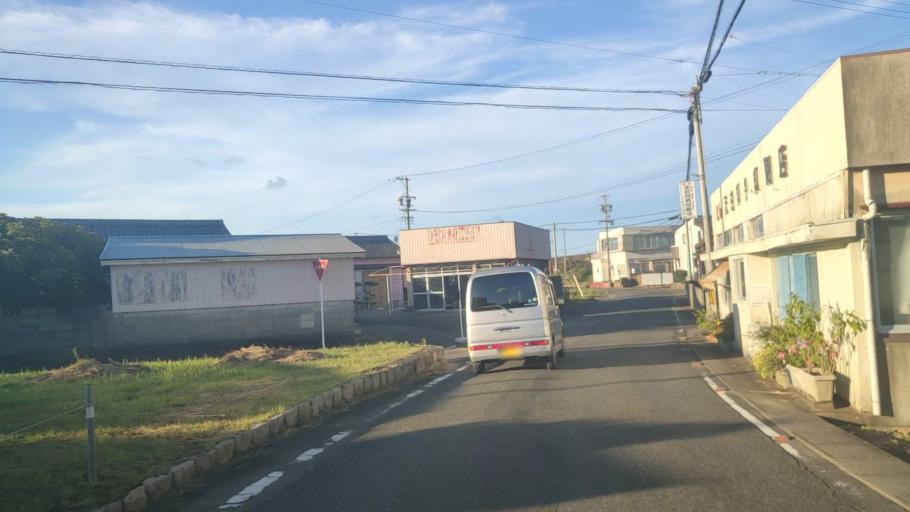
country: JP
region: Mie
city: Toba
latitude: 34.2558
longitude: 136.8466
